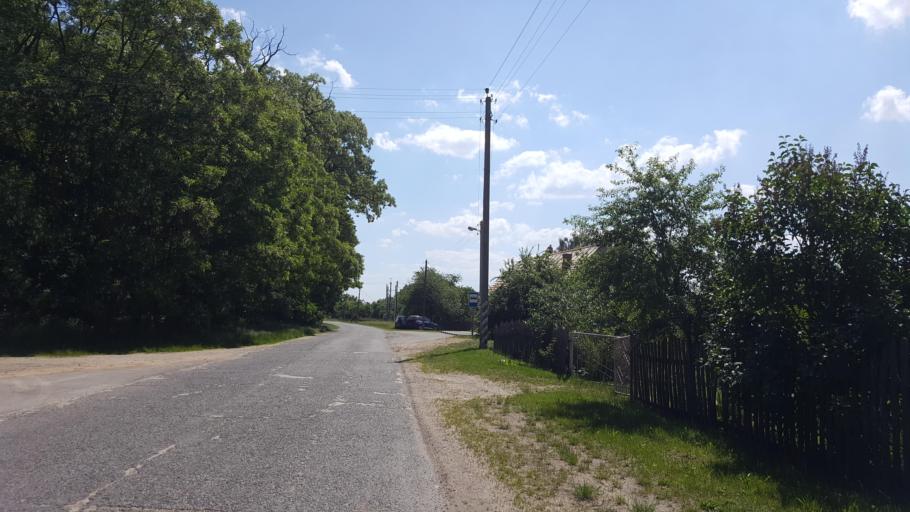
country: BY
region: Brest
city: Zhabinka
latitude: 52.2436
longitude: 24.0238
